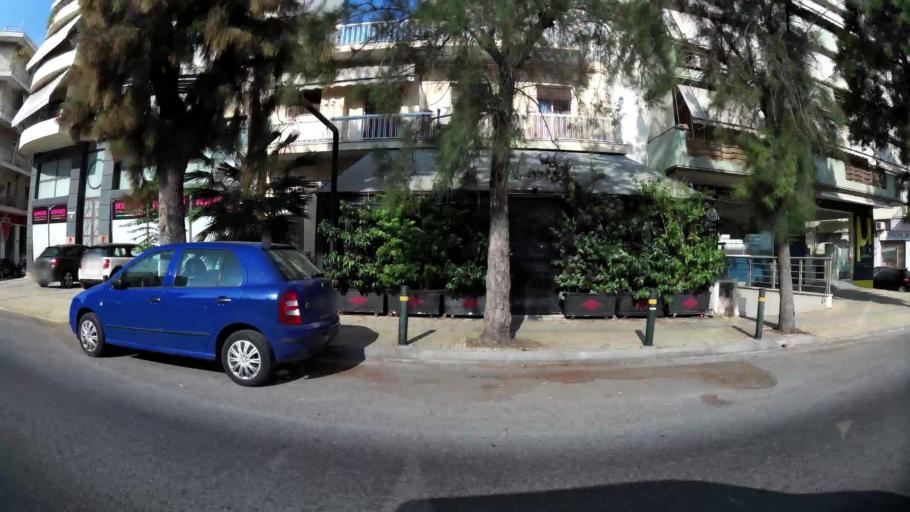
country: GR
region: Attica
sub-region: Nomarchia Athinas
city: Nea Chalkidona
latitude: 38.0213
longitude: 23.7380
